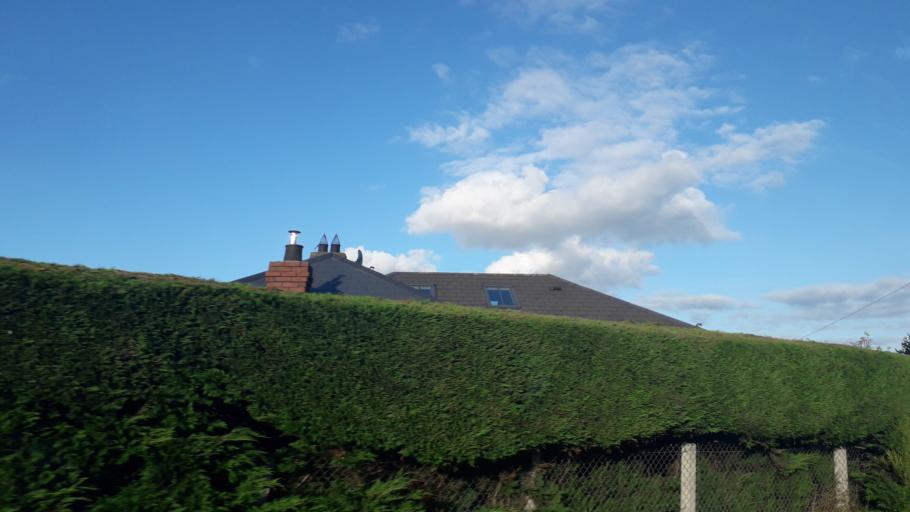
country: IE
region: Leinster
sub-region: Lu
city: Carlingford
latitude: 54.0377
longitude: -6.1738
